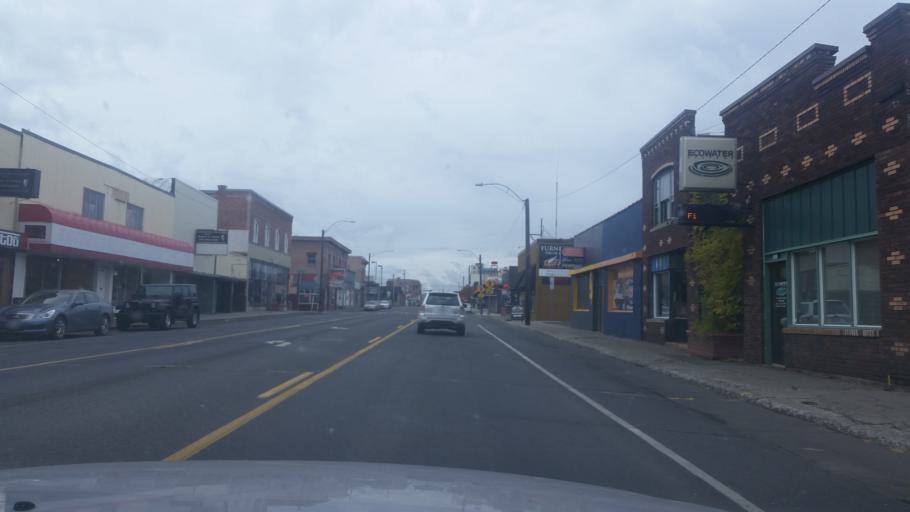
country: US
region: Washington
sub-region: Spokane County
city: Spokane
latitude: 47.6573
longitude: -117.3831
